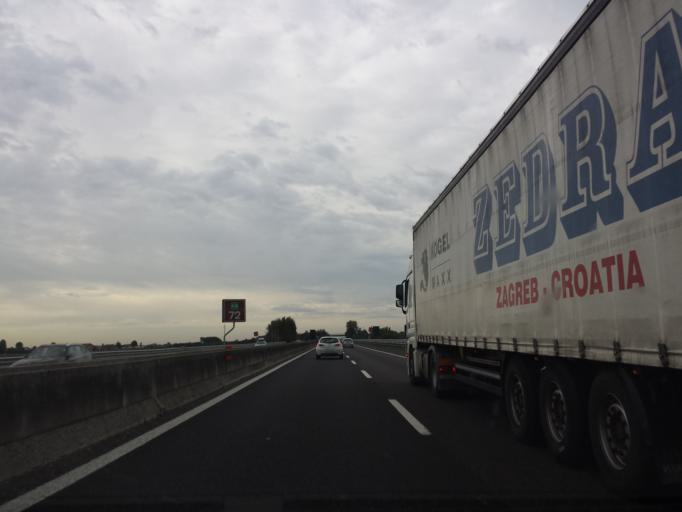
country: IT
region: Veneto
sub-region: Provincia di Padova
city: Pozzonovo
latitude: 45.1913
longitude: 11.7757
